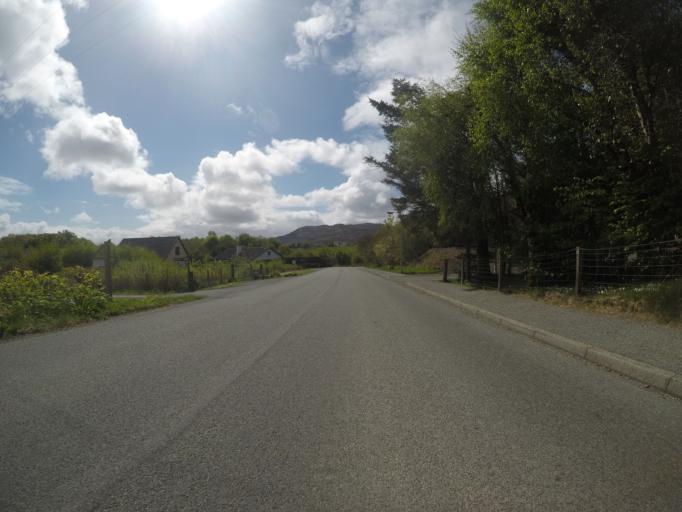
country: GB
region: Scotland
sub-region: Highland
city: Portree
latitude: 57.4209
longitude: -6.1910
